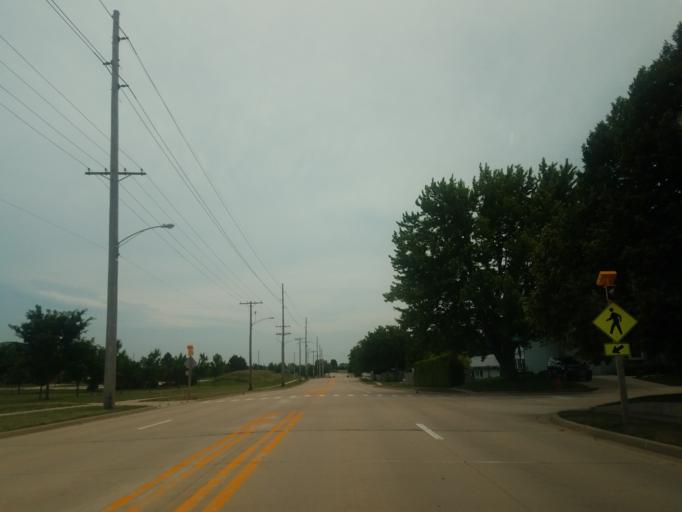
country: US
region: Illinois
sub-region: McLean County
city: Normal
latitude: 40.5216
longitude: -88.9437
